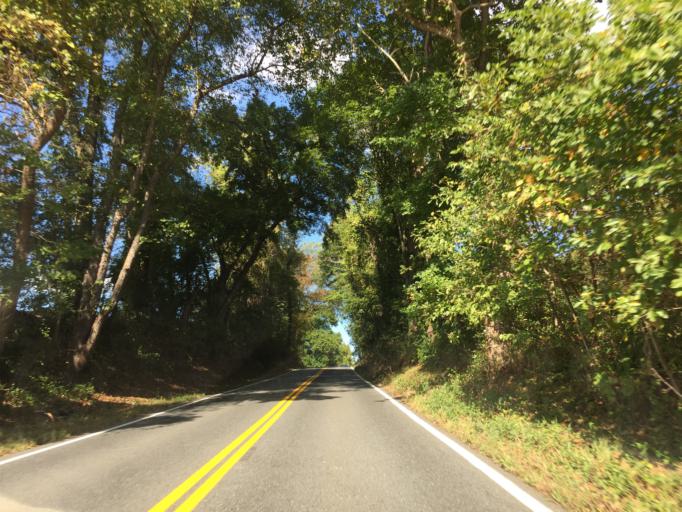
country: US
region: Maryland
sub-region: Harford County
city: Fallston
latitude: 39.5131
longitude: -76.4579
